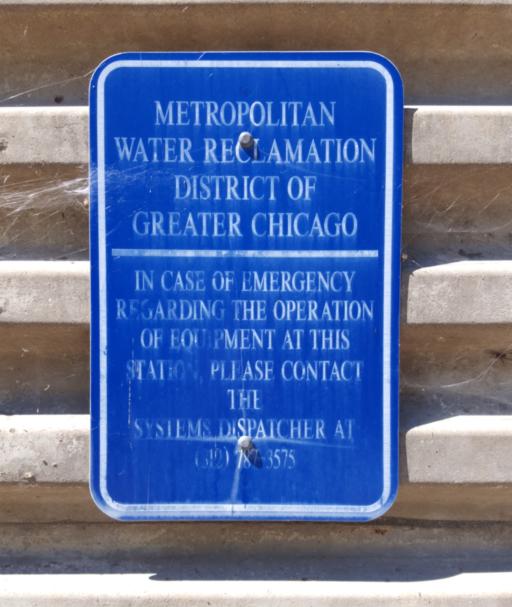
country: US
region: Illinois
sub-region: Cook County
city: Northbrook
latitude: 42.1463
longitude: -87.8143
